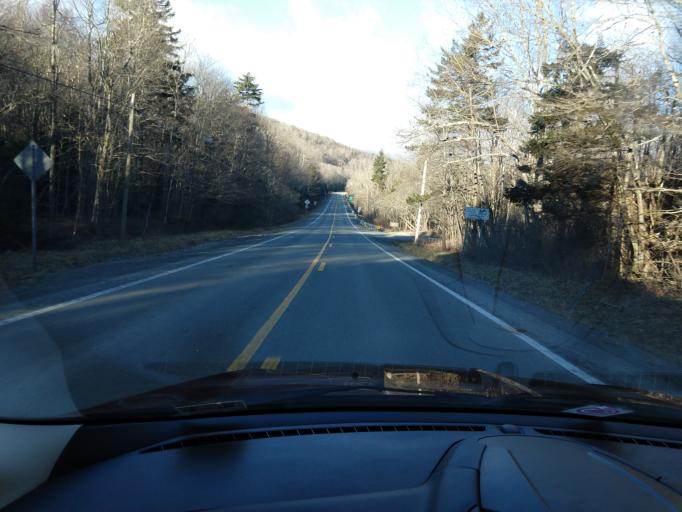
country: US
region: West Virginia
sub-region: Randolph County
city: Elkins
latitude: 38.5998
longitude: -79.8506
